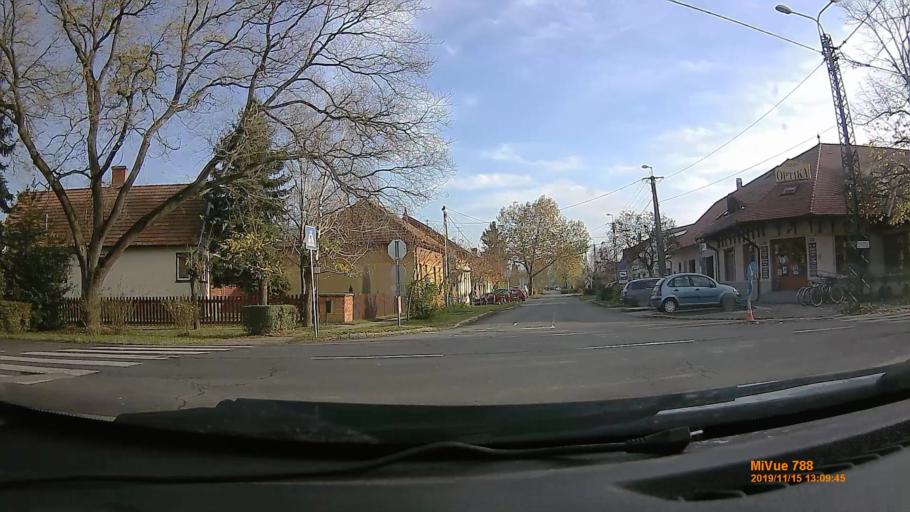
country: HU
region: Bekes
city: Gyula
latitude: 46.6410
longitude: 21.2788
